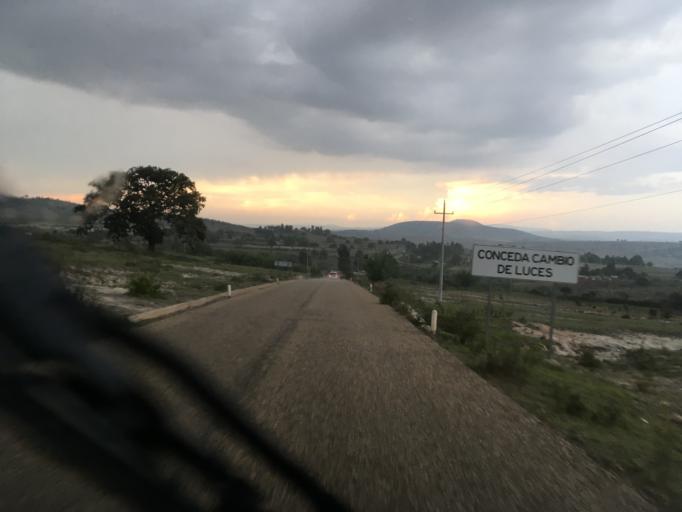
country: MX
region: Oaxaca
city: Santiago Tilantongo
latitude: 17.2827
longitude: -97.2897
